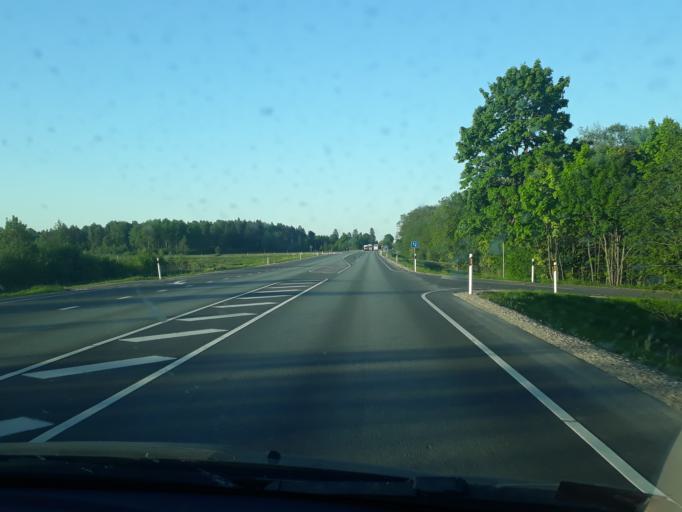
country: EE
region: Paernumaa
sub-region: Tootsi vald
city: Tootsi
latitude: 58.4919
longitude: 24.7601
